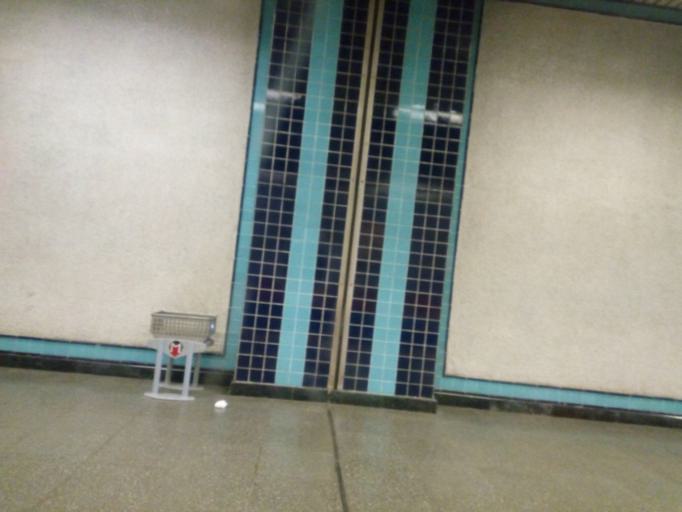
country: TR
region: Istanbul
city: Bahcelievler
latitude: 40.9967
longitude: 28.8750
